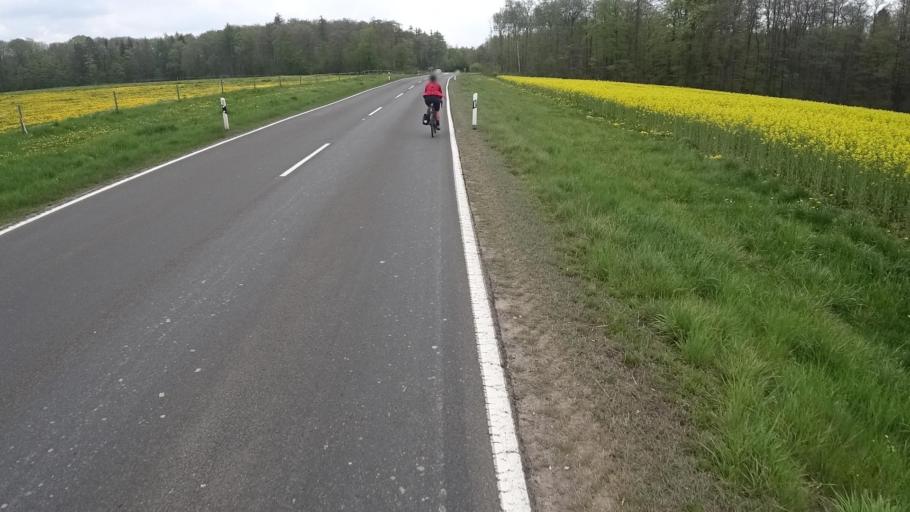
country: DE
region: Rheinland-Pfalz
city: Horn
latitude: 50.0507
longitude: 7.5177
